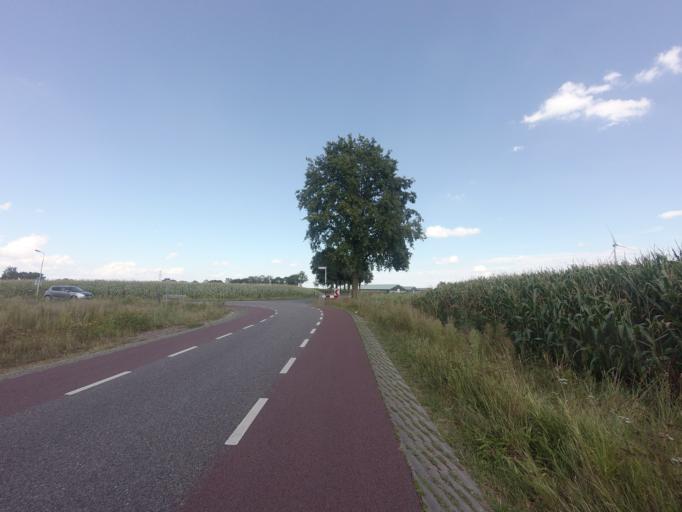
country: NL
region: Overijssel
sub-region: Gemeente Twenterand
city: Den Ham
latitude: 52.5736
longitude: 6.4490
